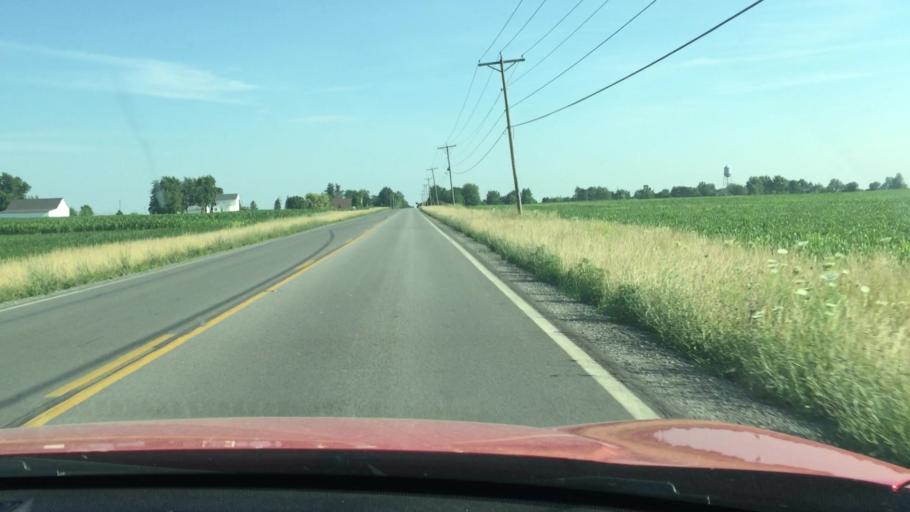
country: US
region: Ohio
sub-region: Hardin County
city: Ada
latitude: 40.7222
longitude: -83.8423
